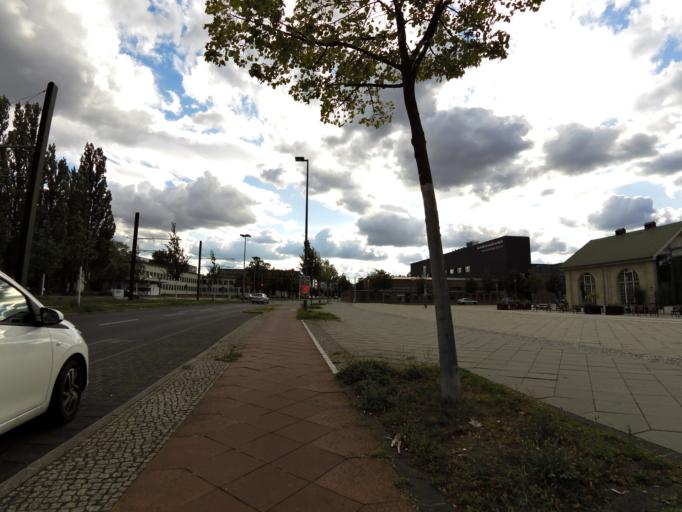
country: DE
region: Berlin
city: Adlershof
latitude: 52.4313
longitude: 13.5334
